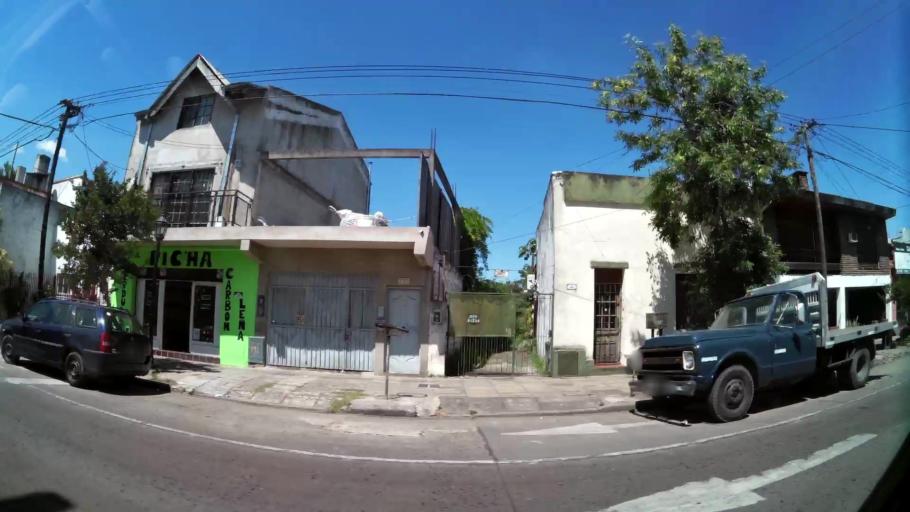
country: AR
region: Buenos Aires
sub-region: Partido de Tigre
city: Tigre
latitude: -34.4267
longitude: -58.5707
